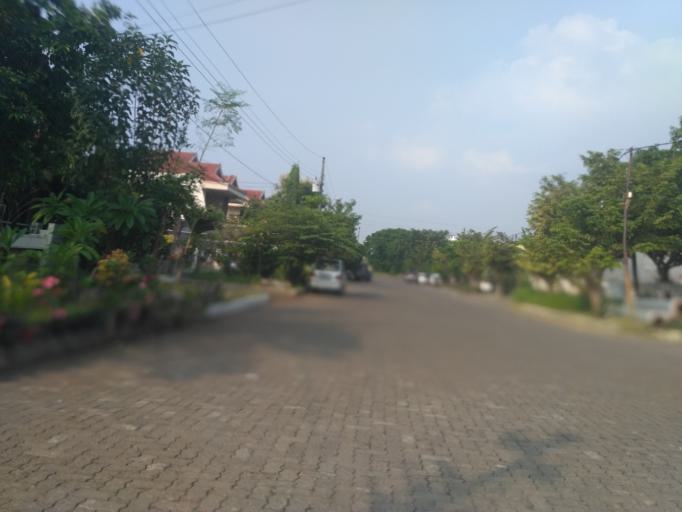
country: ID
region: Central Java
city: Semarang
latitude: -6.9677
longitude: 110.3844
